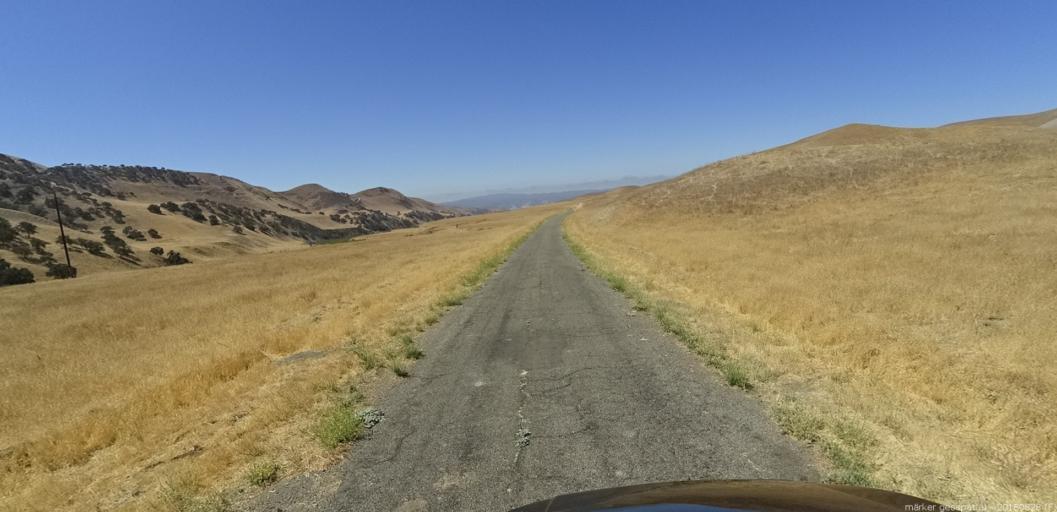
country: US
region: California
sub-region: San Luis Obispo County
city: San Miguel
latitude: 36.0612
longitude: -120.7999
